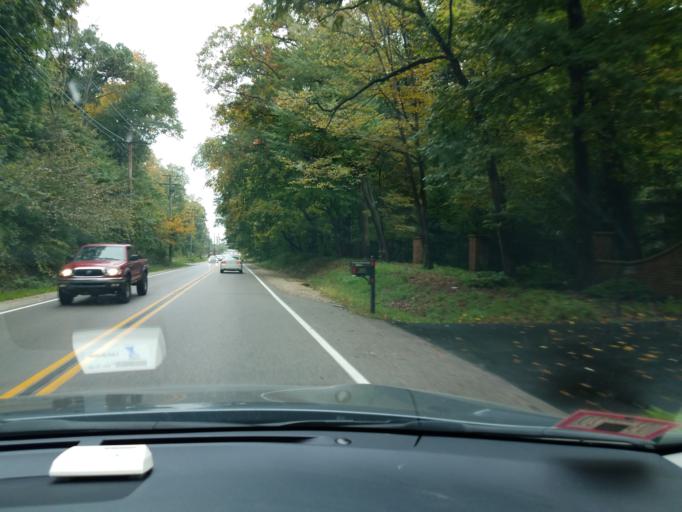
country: US
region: Illinois
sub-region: Lake County
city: Riverwoods
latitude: 42.1676
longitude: -87.9082
